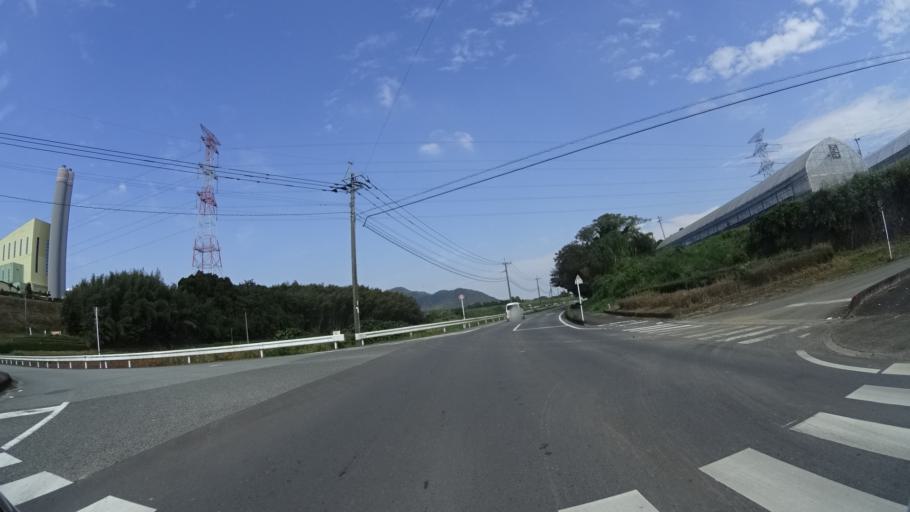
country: JP
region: Kumamoto
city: Matsubase
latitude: 32.6602
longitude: 130.7154
